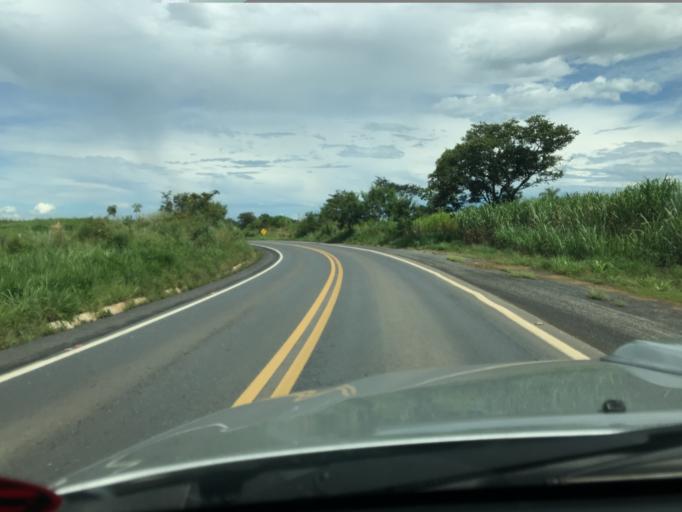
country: BR
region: Minas Gerais
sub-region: Campos Altos
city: Campos Altos
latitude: -19.8108
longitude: -46.0328
